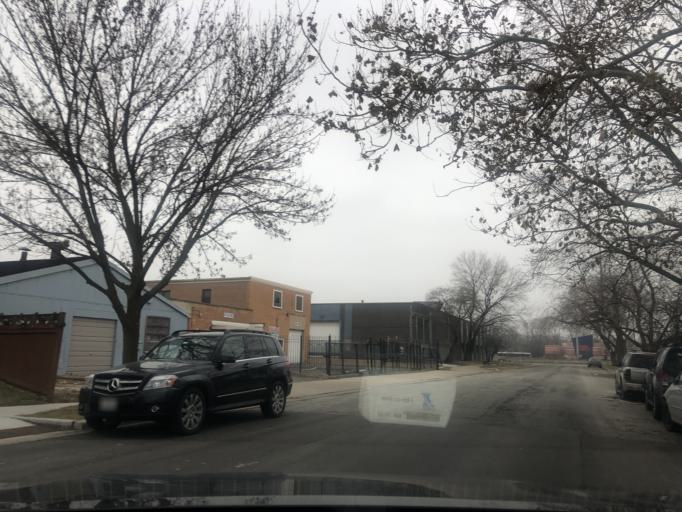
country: US
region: Illinois
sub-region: Cook County
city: Calumet Park
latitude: 41.7328
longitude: -87.6225
